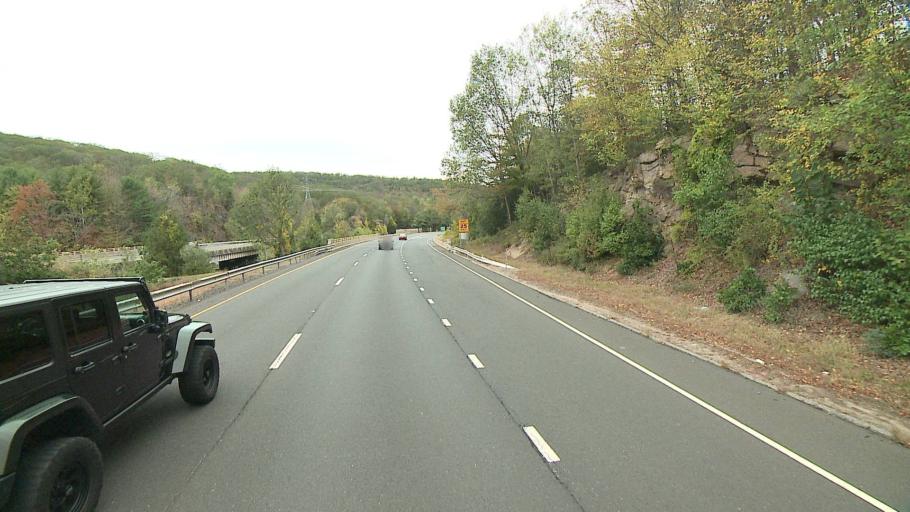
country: US
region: Connecticut
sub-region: Middlesex County
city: Higganum
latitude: 41.4708
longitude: -72.5555
